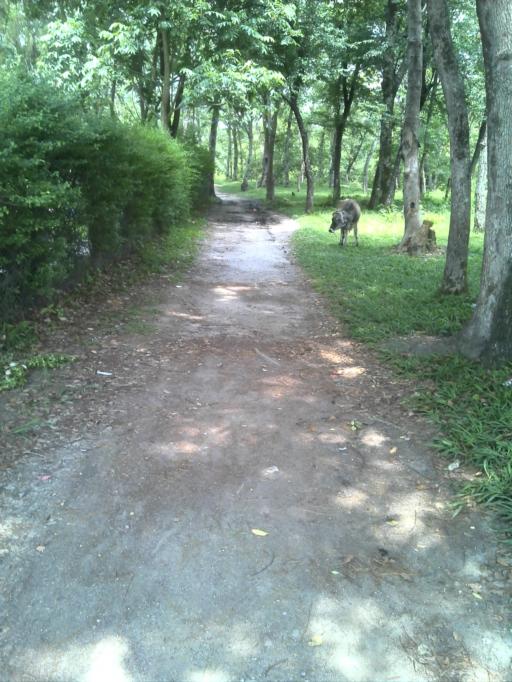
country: NP
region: Central Region
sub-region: Bagmati Zone
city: Bhaktapur
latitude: 27.7244
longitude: 85.4528
